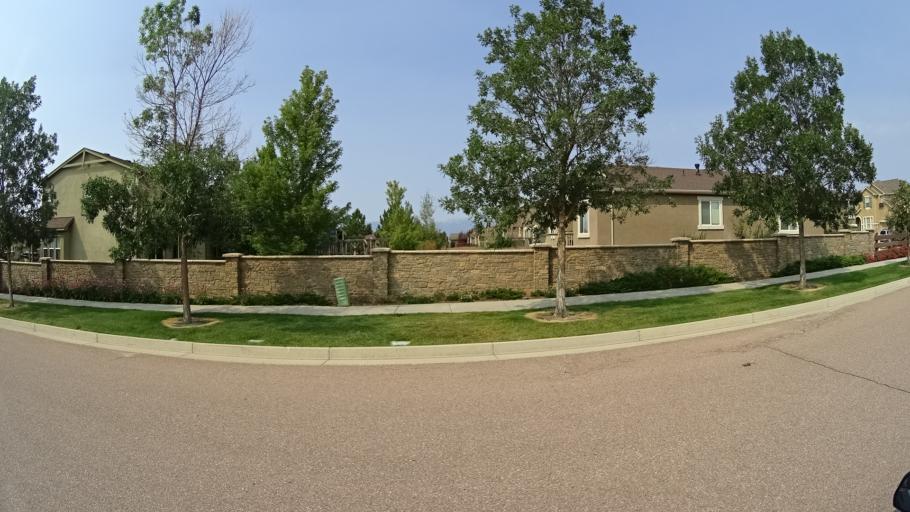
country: US
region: Colorado
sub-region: El Paso County
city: Black Forest
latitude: 38.9671
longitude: -104.7342
